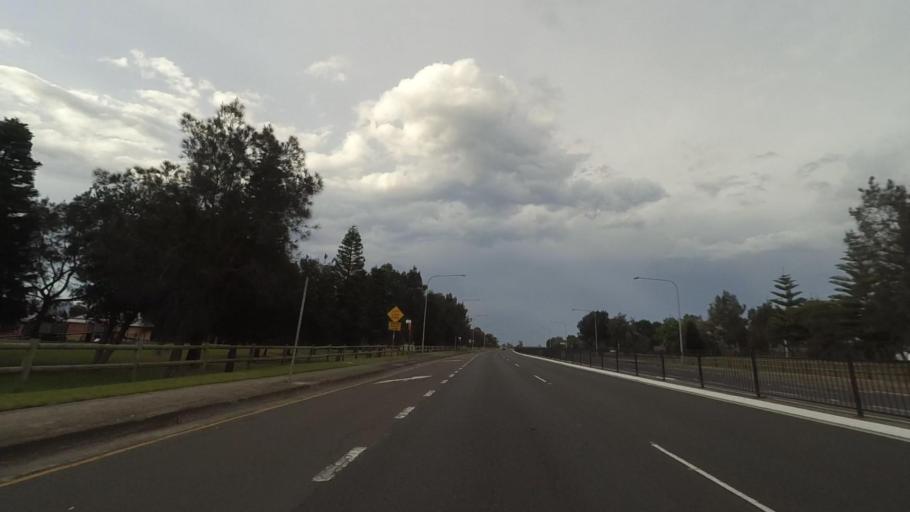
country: AU
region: New South Wales
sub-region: Shellharbour
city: Lake Illawarra
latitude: -34.5402
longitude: 150.8647
